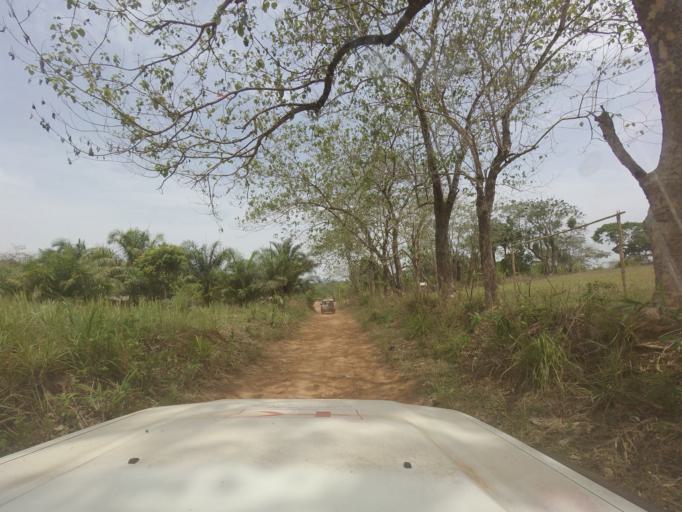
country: SL
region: Eastern Province
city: Buedu
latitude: 8.4761
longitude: -10.3360
